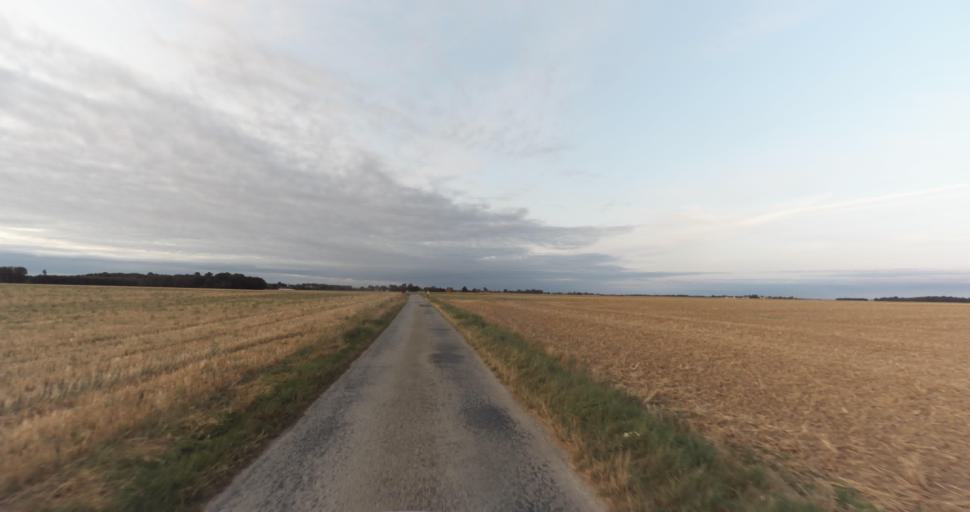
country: FR
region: Haute-Normandie
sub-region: Departement de l'Eure
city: La Madeleine-de-Nonancourt
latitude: 48.8668
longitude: 1.1934
